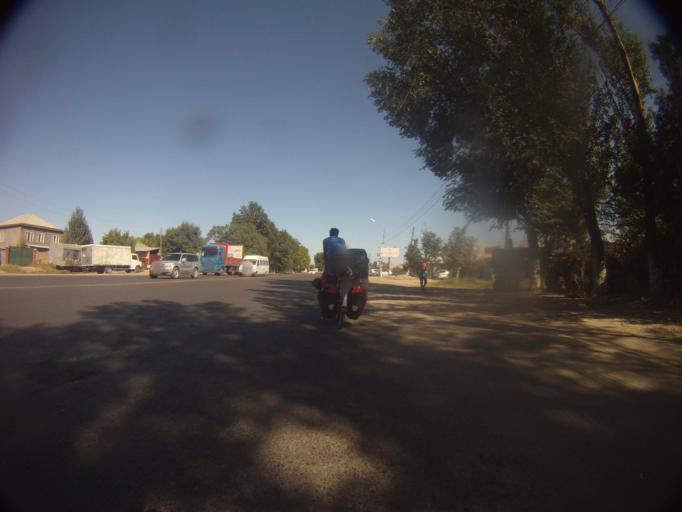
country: KG
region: Chuy
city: Bishkek
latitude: 42.8732
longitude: 74.4527
